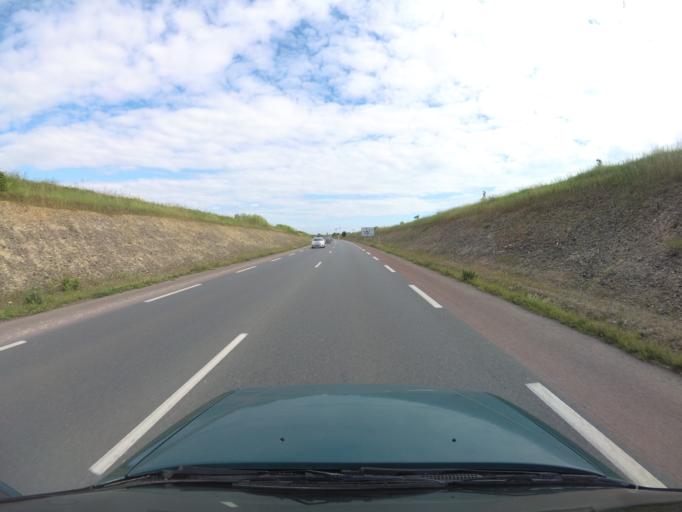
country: FR
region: Poitou-Charentes
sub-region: Departement de la Charente-Maritime
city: Saint-Xandre
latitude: 46.1846
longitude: -1.0930
